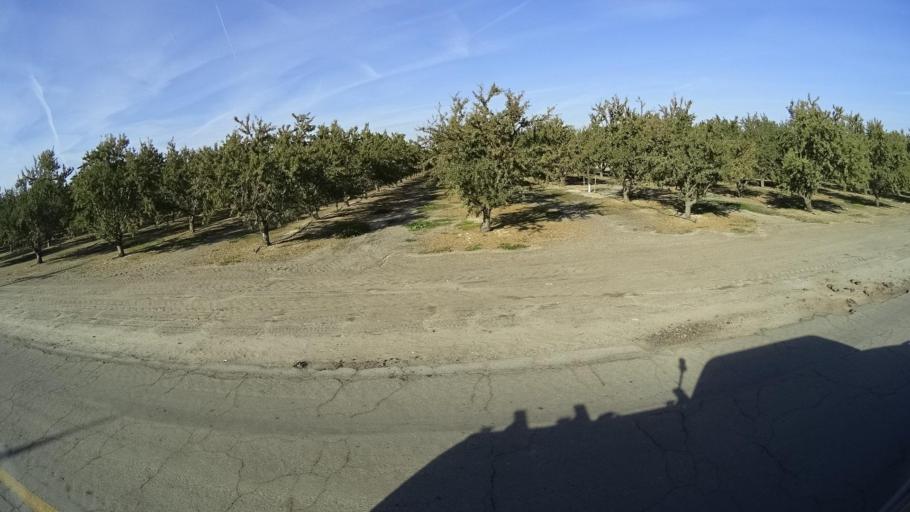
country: US
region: California
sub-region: Kern County
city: McFarland
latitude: 35.7034
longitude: -119.2362
